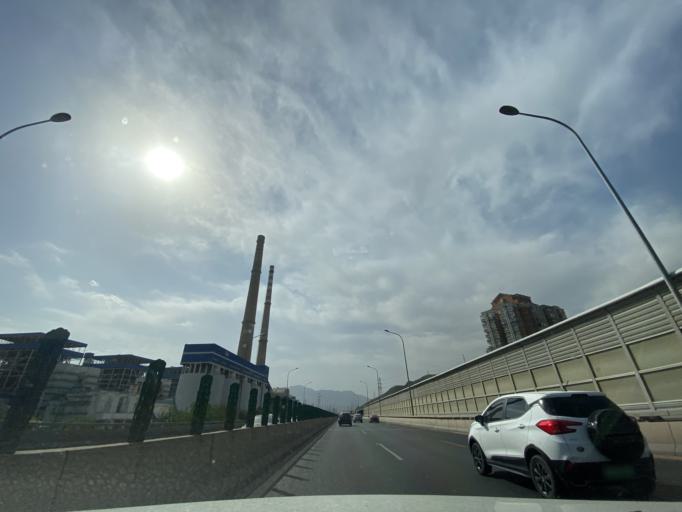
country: CN
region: Beijing
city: Guangning
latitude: 39.9233
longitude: 116.1417
